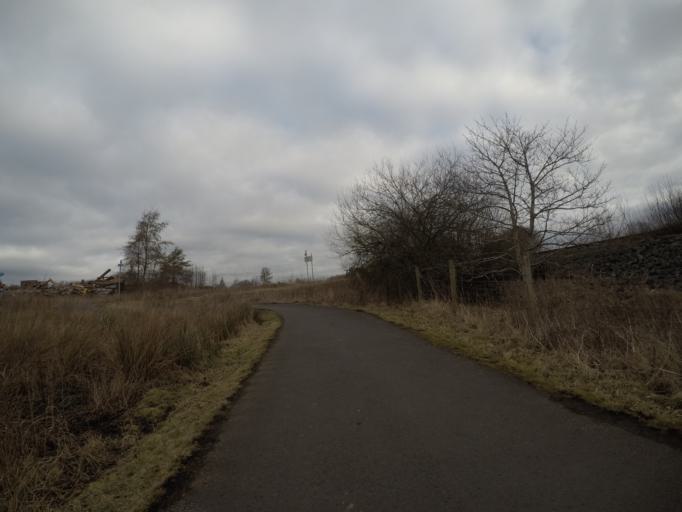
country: GB
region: Scotland
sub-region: North Ayrshire
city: Dreghorn
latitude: 55.5718
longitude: -4.6361
